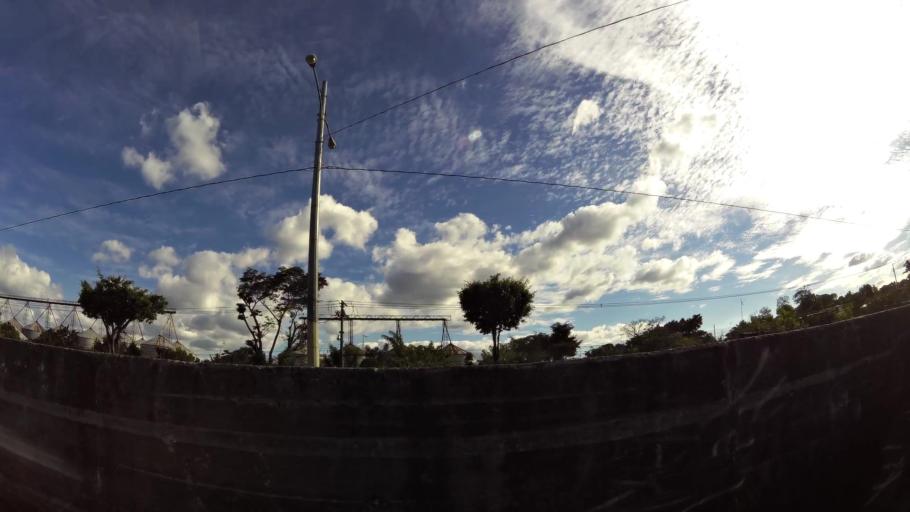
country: SV
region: San Salvador
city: Ilopango
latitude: 13.7352
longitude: -89.0579
